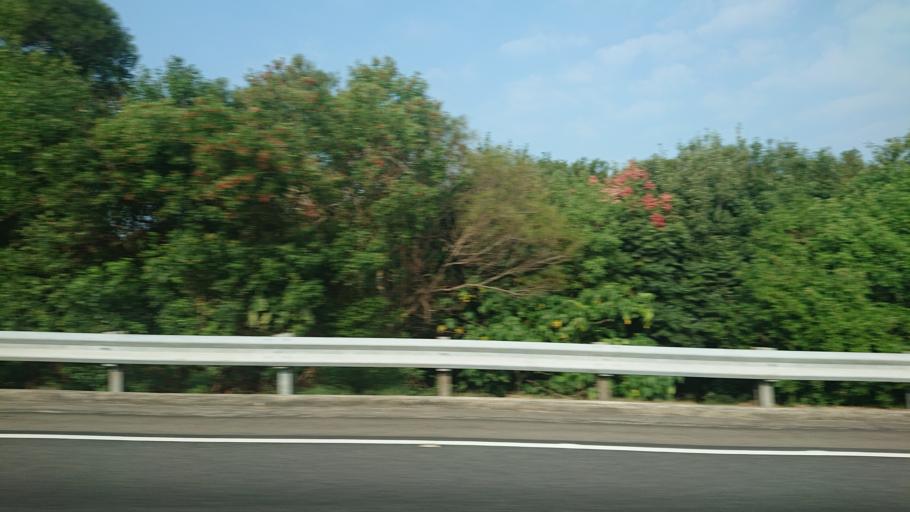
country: TW
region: Taiwan
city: Fengyuan
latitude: 24.2828
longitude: 120.5997
